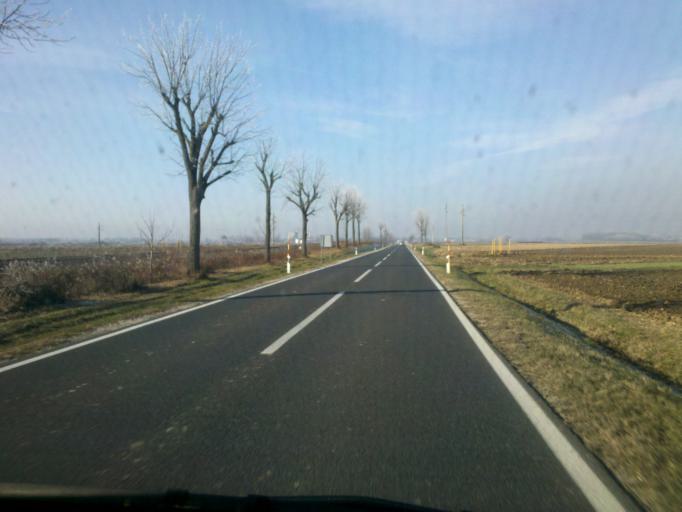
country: HR
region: Koprivnicko-Krizevacka
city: Kalinovac
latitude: 46.0141
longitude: 17.0944
